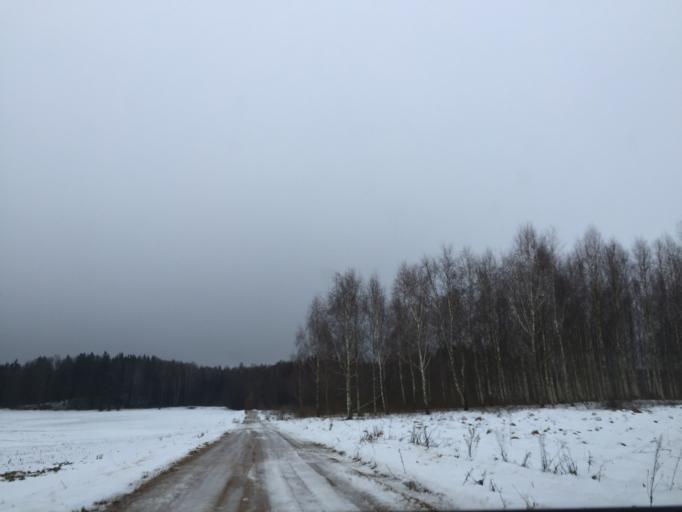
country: LV
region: Krimulda
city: Ragana
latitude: 57.1616
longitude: 24.7570
